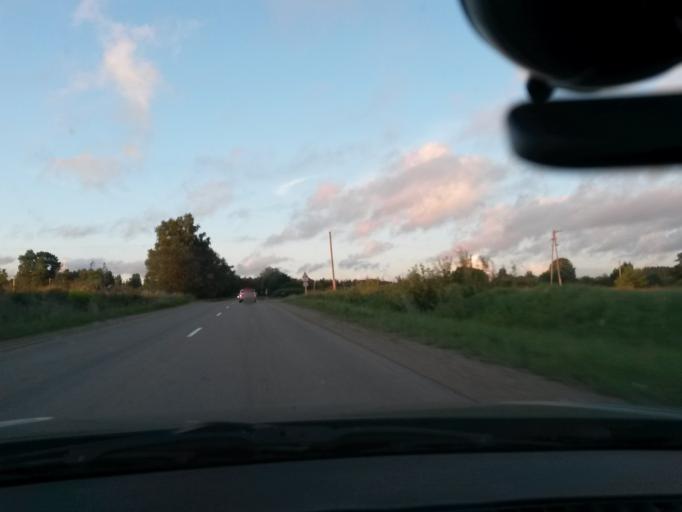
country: LV
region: Madonas Rajons
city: Madona
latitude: 56.8022
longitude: 26.0395
